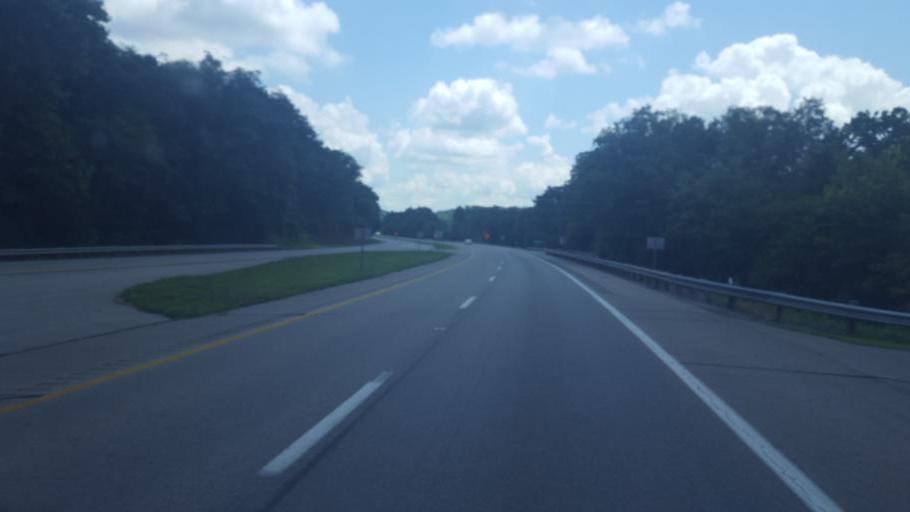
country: US
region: Ohio
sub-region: Jackson County
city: Jackson
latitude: 39.1337
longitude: -82.7142
